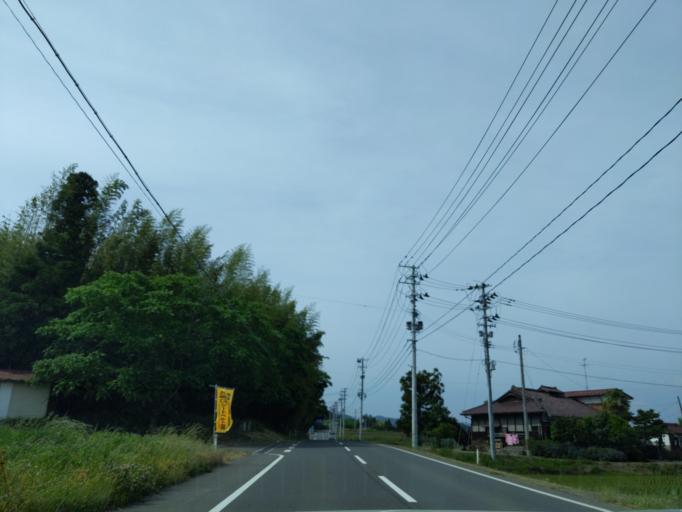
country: JP
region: Fukushima
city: Koriyama
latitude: 37.4579
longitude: 140.3126
